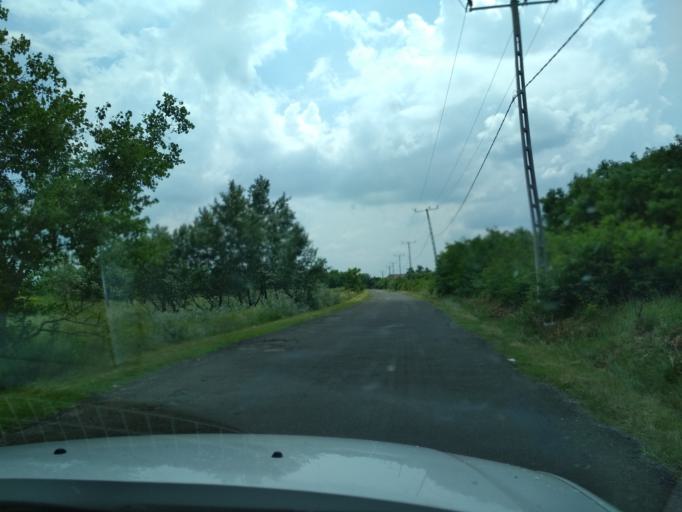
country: HU
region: Pest
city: Nagykata
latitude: 47.3782
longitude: 19.7574
